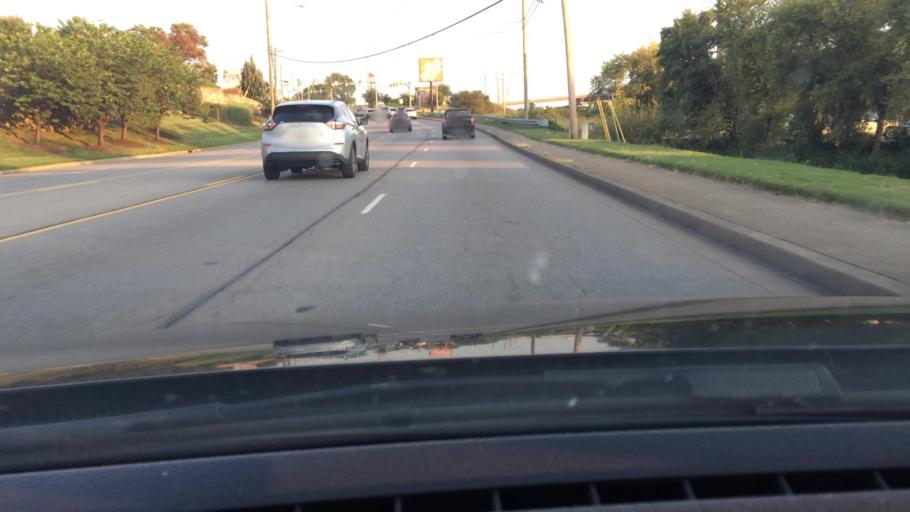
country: US
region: Tennessee
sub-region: Davidson County
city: Oak Hill
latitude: 36.1079
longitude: -86.7656
